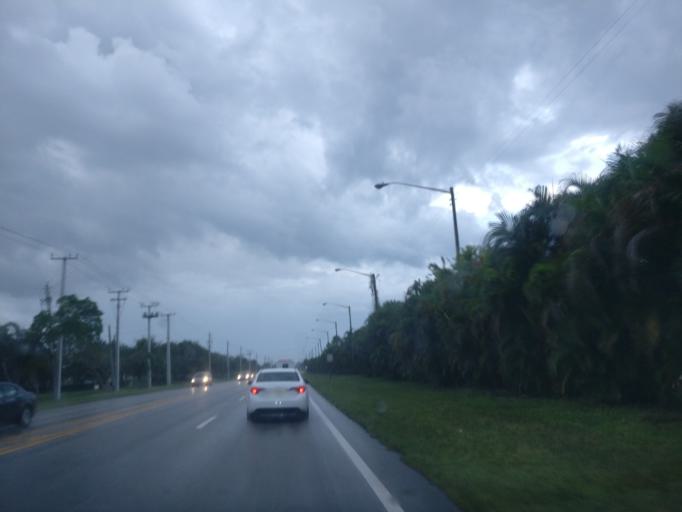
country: US
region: Florida
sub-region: Palm Beach County
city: Schall Circle
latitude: 26.7190
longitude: -80.1189
